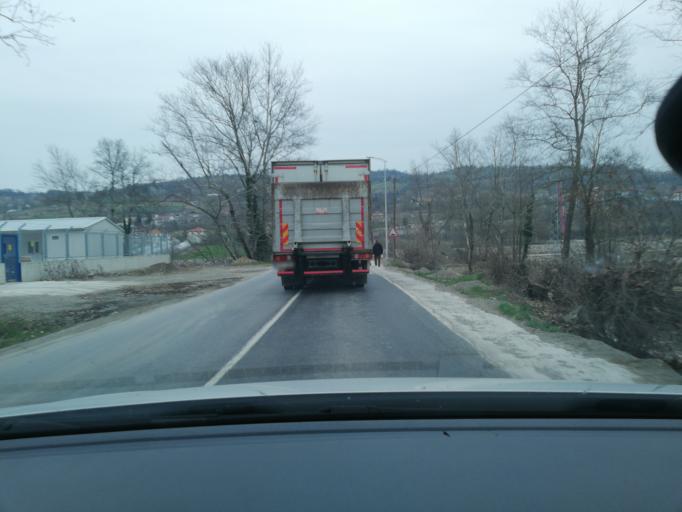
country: TR
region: Zonguldak
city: Gokcebey
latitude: 41.3050
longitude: 32.1263
